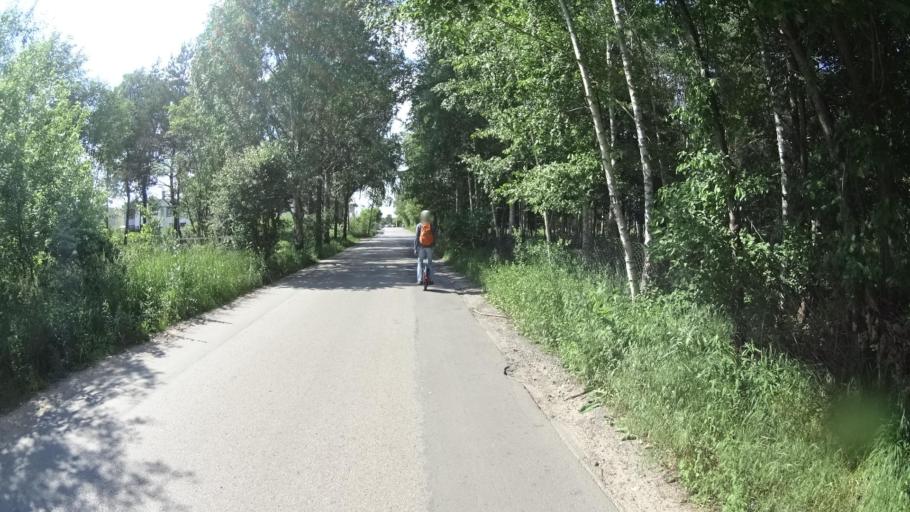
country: PL
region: Masovian Voivodeship
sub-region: Powiat piaseczynski
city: Jozefoslaw
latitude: 52.0977
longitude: 21.0712
